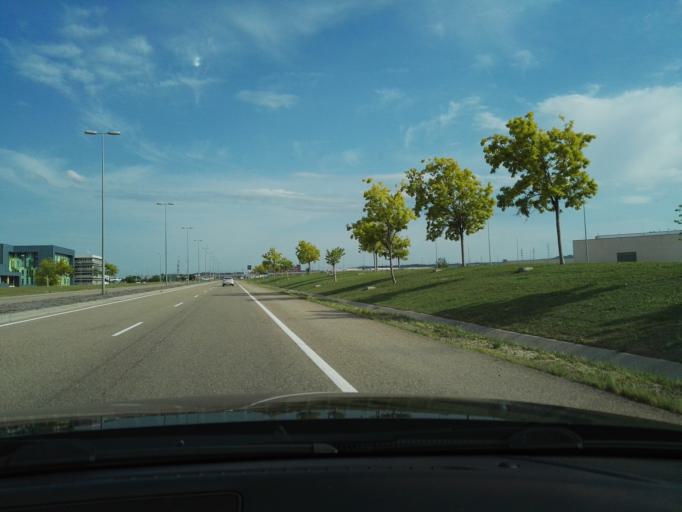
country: ES
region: Aragon
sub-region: Provincia de Zaragoza
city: Montecanal
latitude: 41.6435
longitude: -0.9946
